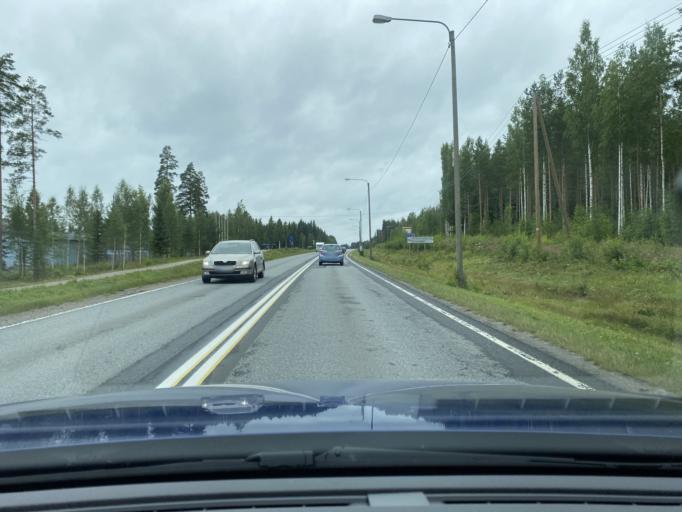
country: FI
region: Central Finland
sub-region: Keuruu
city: Keuruu
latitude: 62.2431
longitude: 24.4798
